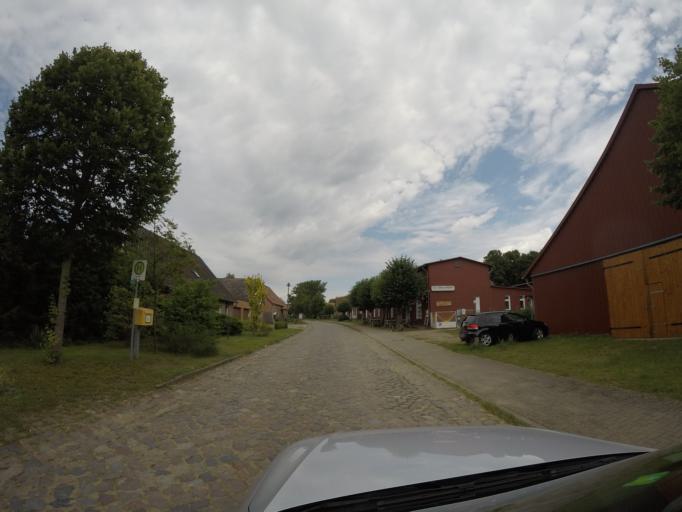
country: DE
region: Mecklenburg-Vorpommern
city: Mollenhagen
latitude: 53.4225
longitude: 12.9307
